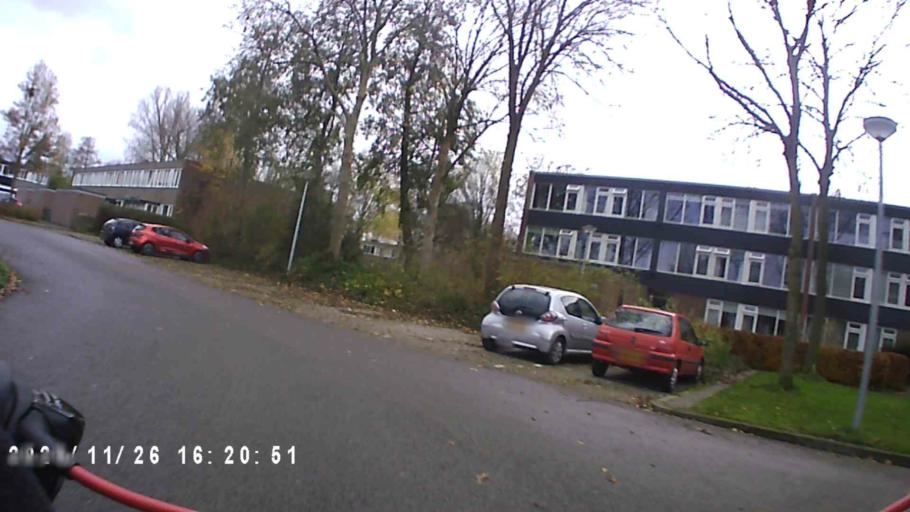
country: NL
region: Groningen
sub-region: Gemeente Groningen
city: Oosterpark
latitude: 53.2331
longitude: 6.6247
